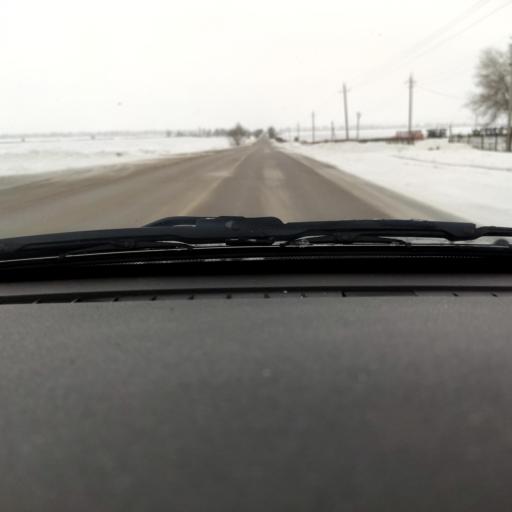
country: RU
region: Voronezj
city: Novaya Usman'
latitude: 51.5809
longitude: 39.3748
